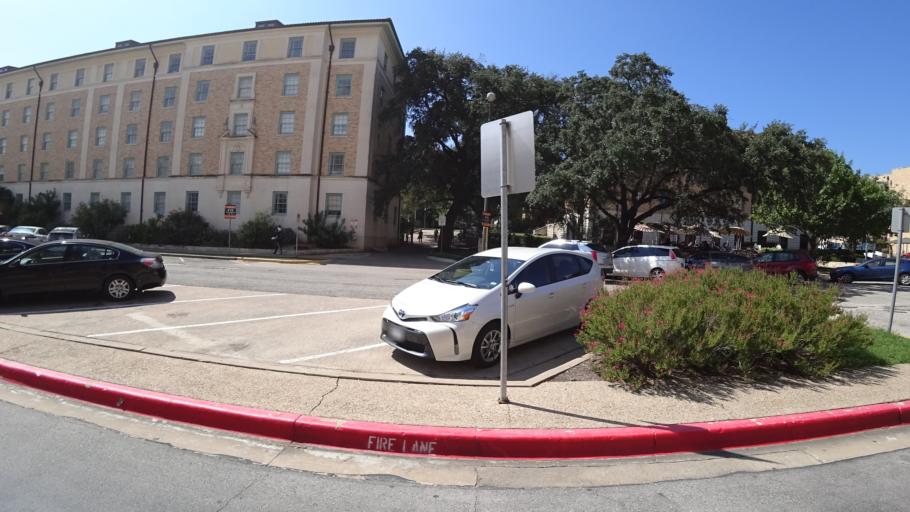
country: US
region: Texas
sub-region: Travis County
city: Austin
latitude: 30.2890
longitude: -97.7390
